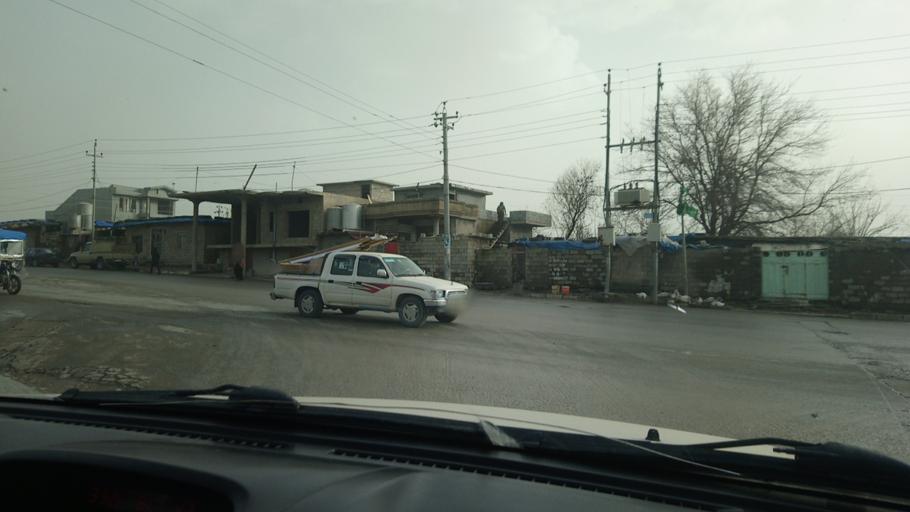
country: IQ
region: As Sulaymaniyah
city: Qeladize
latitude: 36.1785
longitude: 45.1445
